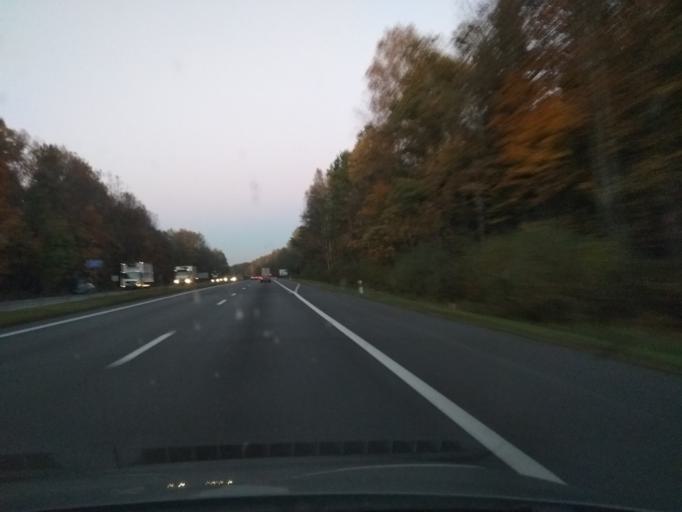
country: BY
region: Minsk
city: Enyerhyetykaw
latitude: 53.5851
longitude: 27.0315
